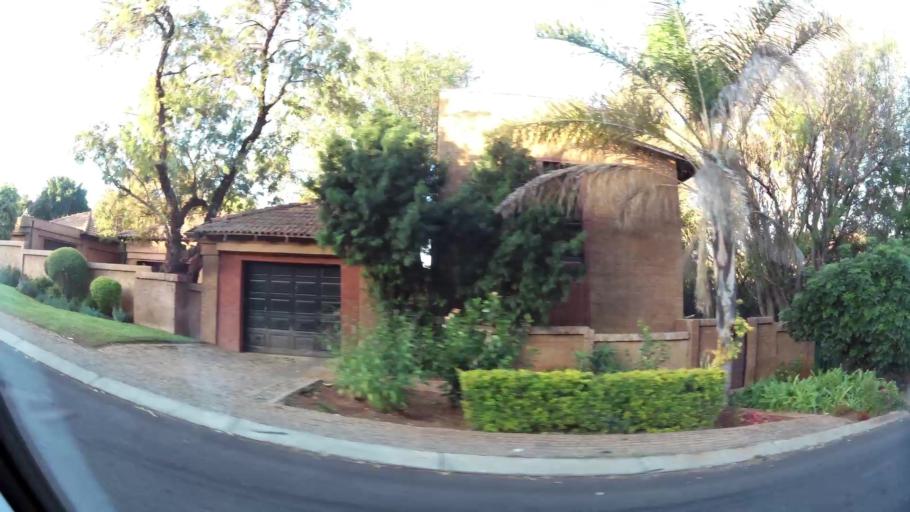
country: ZA
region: North-West
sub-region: Bojanala Platinum District Municipality
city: Rustenburg
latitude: -25.7091
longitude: 27.2411
